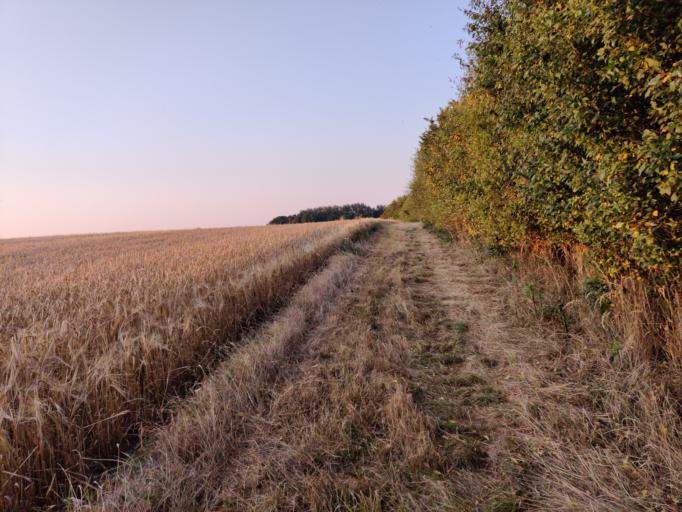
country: DK
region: South Denmark
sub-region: AEro Kommune
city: AEroskobing
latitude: 54.8994
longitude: 10.3124
